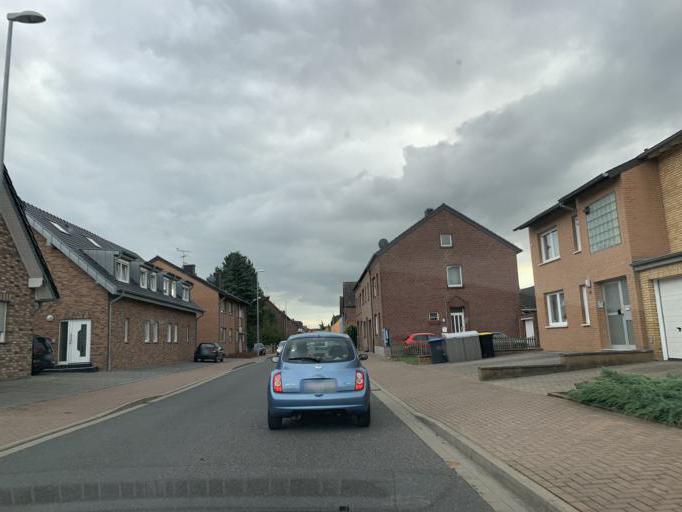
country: DE
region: North Rhine-Westphalia
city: Huckelhoven
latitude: 51.0390
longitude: 6.2158
